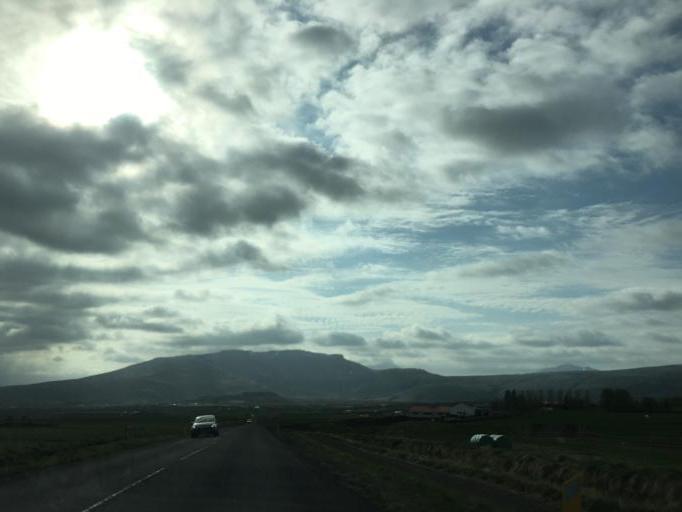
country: IS
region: South
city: Selfoss
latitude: 64.3088
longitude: -20.2204
